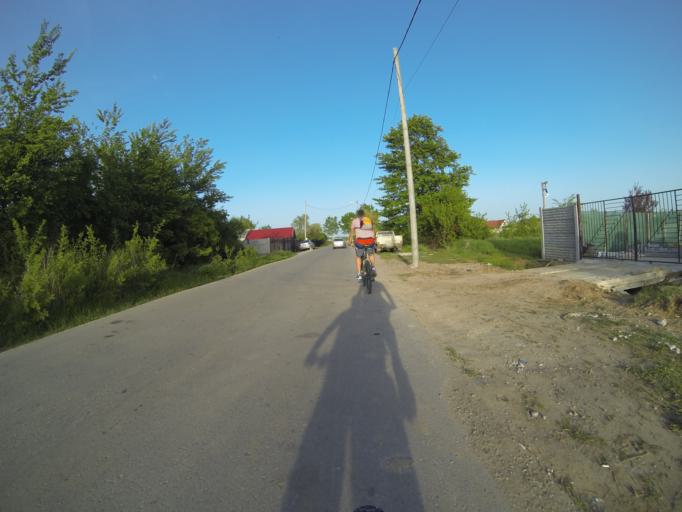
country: RO
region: Dolj
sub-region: Comuna Malu Mare
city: Preajba
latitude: 44.3226
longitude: 23.8694
